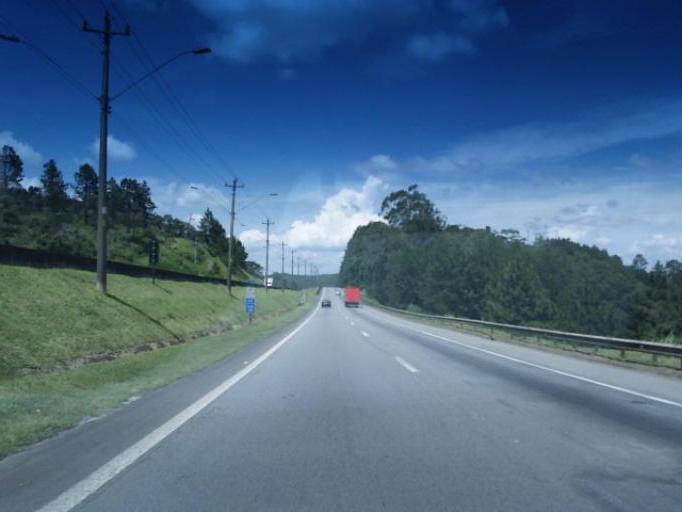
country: BR
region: Sao Paulo
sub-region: Sao Lourenco Da Serra
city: Sao Lourenco da Serra
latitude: -23.8694
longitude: -46.9573
